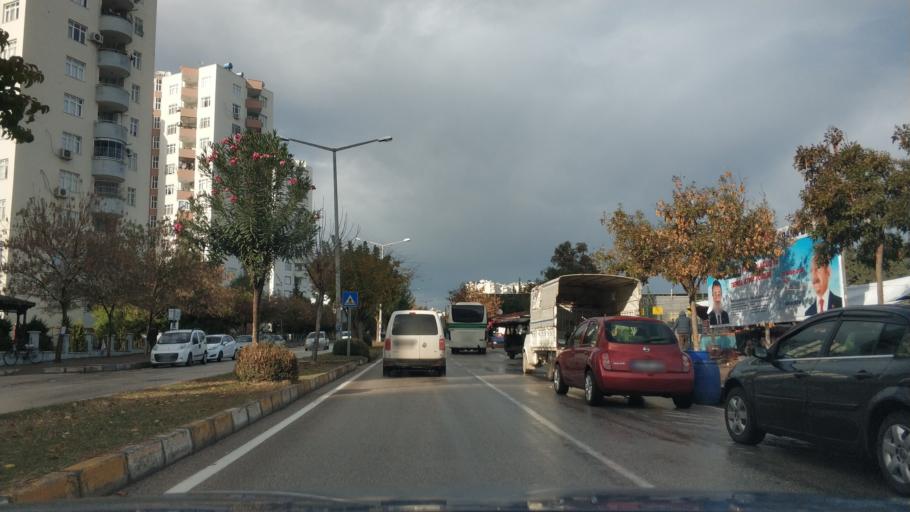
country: TR
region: Adana
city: Seyhan
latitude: 37.0411
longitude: 35.2608
